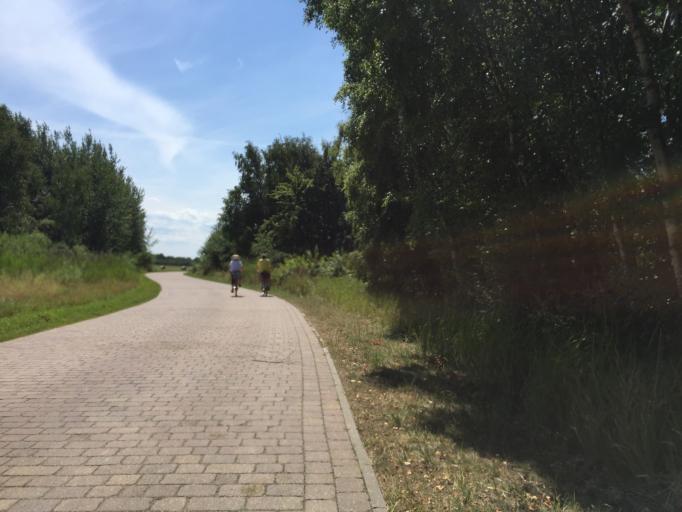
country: DE
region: Mecklenburg-Vorpommern
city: Hiddensee
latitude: 54.5398
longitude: 13.0990
